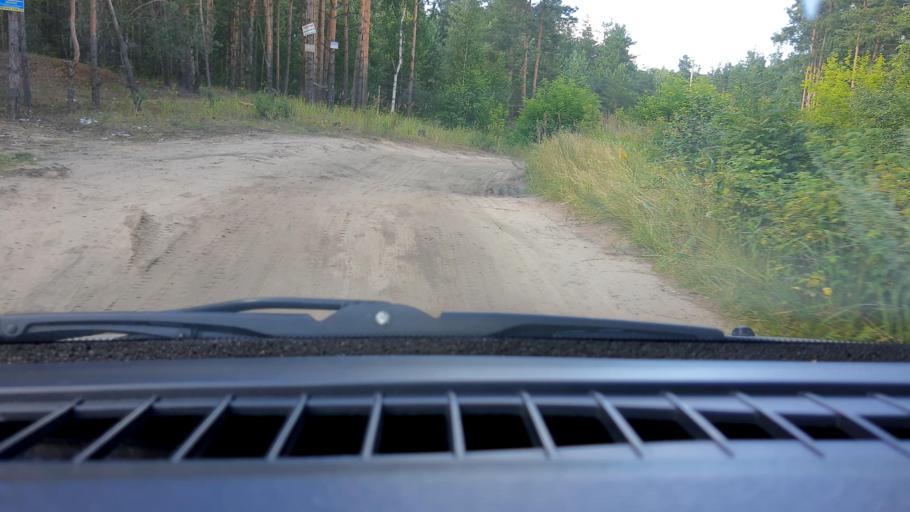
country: RU
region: Nizjnij Novgorod
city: Babino
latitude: 56.3090
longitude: 43.6320
